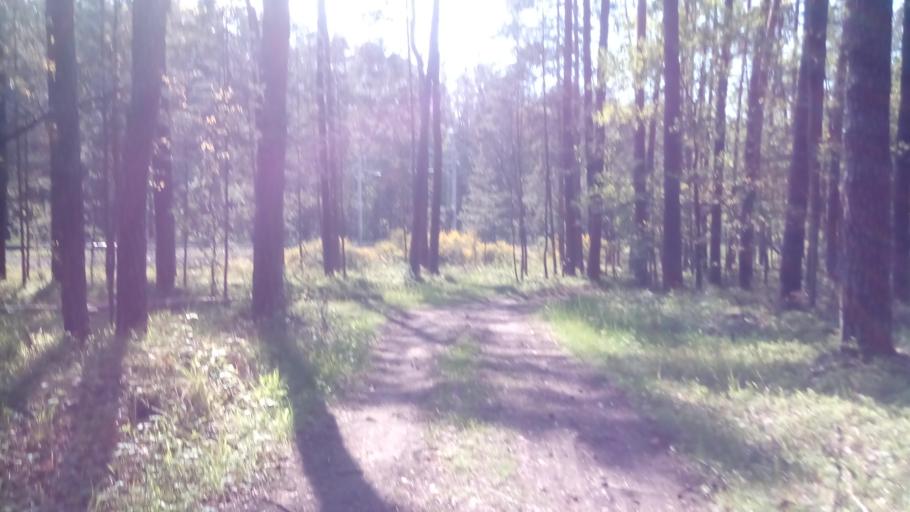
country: PL
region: Opole Voivodeship
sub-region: Powiat opolski
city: Tarnow Opolski
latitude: 50.5849
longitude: 18.0550
